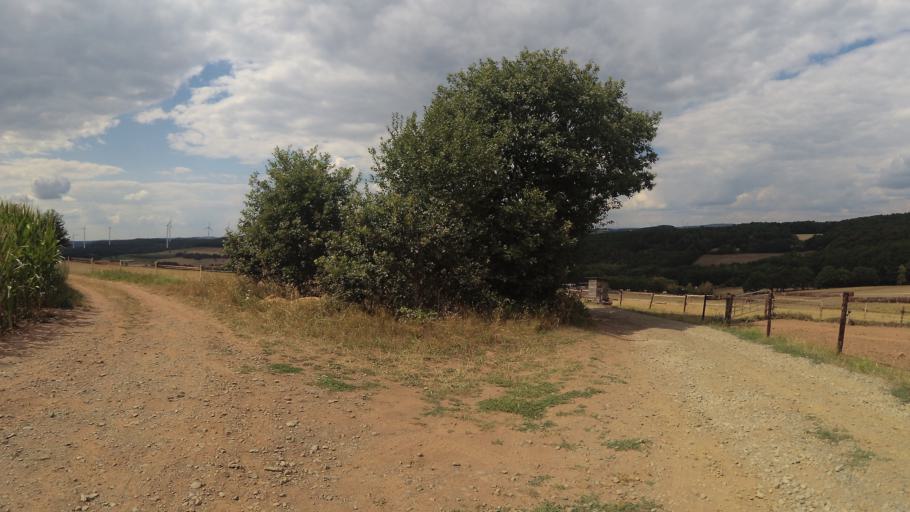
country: DE
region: Rheinland-Pfalz
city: Breitenbach
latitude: 49.4311
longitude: 7.2530
